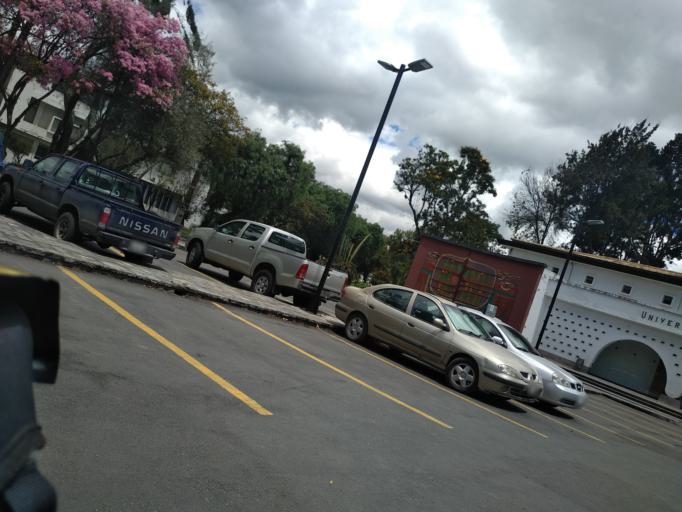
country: EC
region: Azuay
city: Cuenca
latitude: -2.9001
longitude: -79.0096
